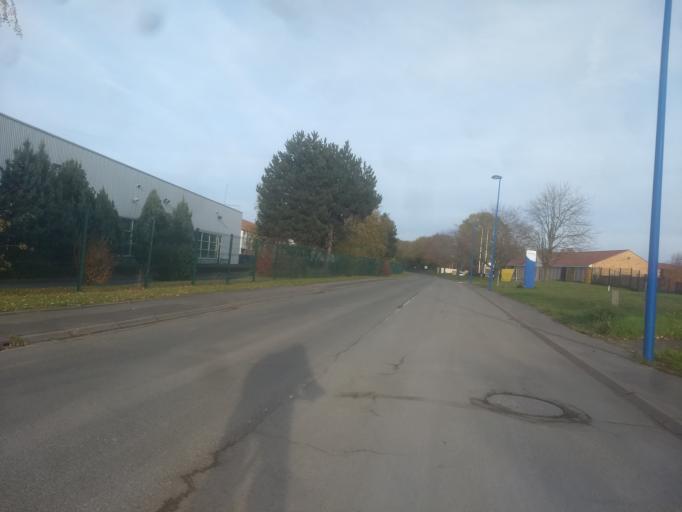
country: FR
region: Nord-Pas-de-Calais
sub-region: Departement du Pas-de-Calais
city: Beaurains
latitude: 50.2569
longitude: 2.7799
